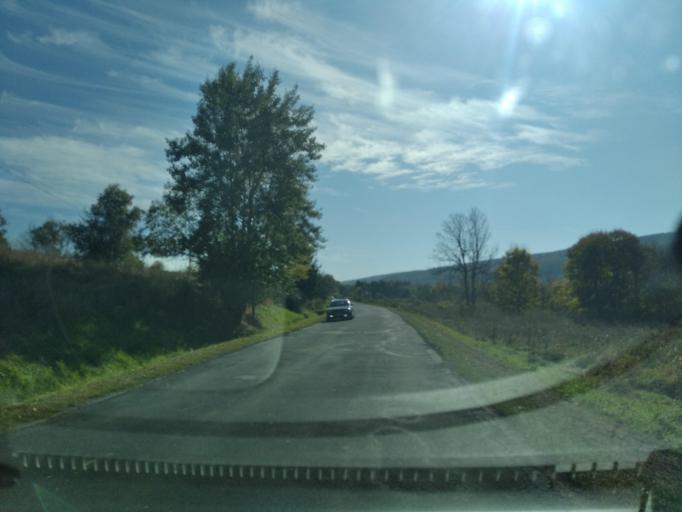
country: PL
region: Subcarpathian Voivodeship
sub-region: Powiat sanocki
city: Komancza
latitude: 49.3978
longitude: 21.9811
